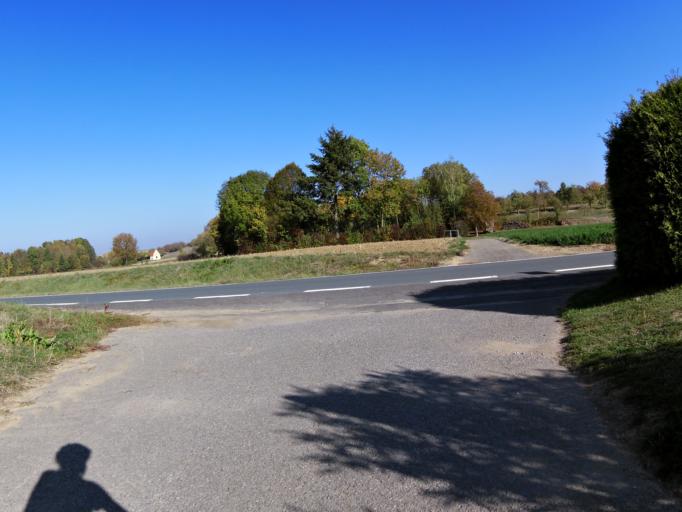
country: DE
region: Bavaria
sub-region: Regierungsbezirk Unterfranken
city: Geroldshausen
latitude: 49.6959
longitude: 9.9258
